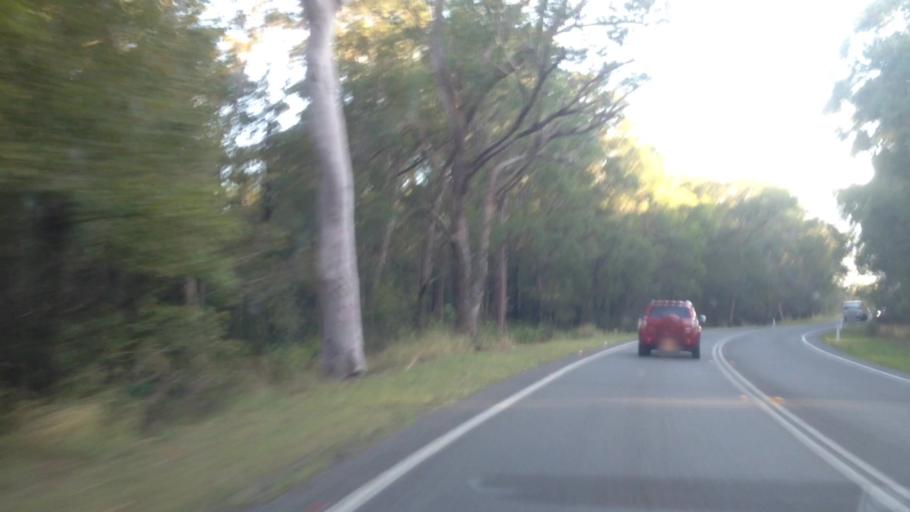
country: AU
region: New South Wales
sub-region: Lake Macquarie Shire
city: Dora Creek
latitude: -33.0005
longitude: 151.4920
